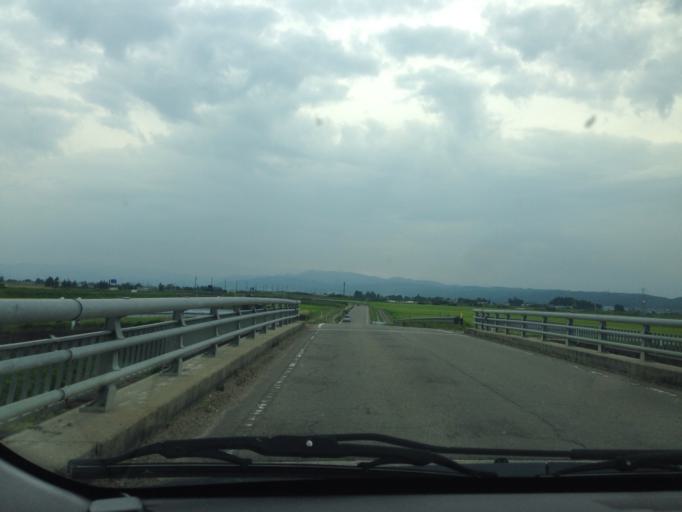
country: JP
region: Fukushima
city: Kitakata
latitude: 37.6047
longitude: 139.8429
